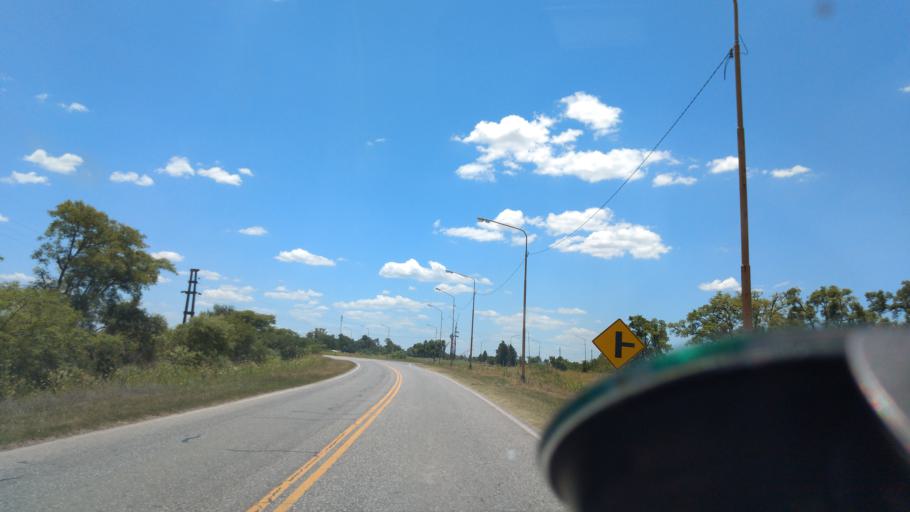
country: AR
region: Santa Fe
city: Laguna Paiva
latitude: -31.3285
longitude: -60.6595
